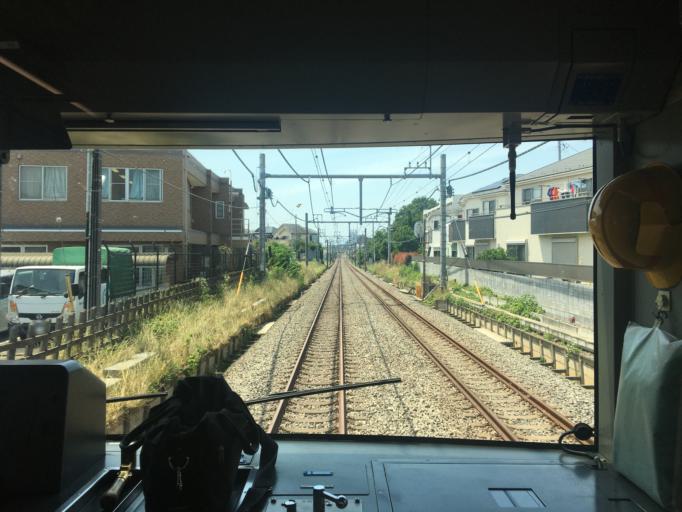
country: JP
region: Tokyo
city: Higashimurayama-shi
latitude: 35.7756
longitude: 139.5072
